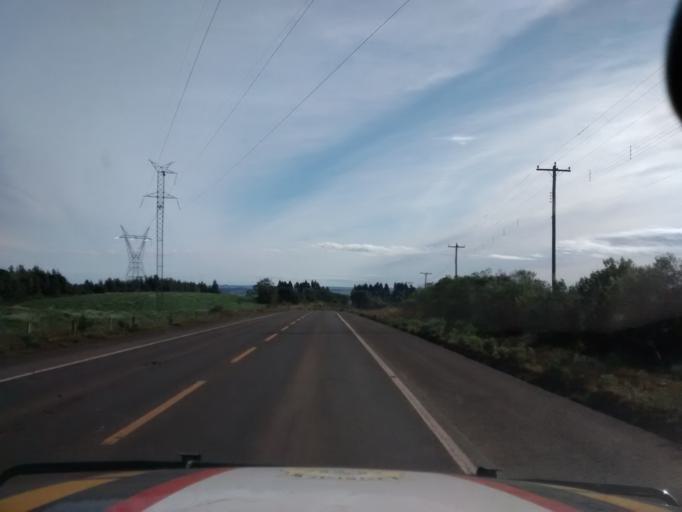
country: BR
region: Rio Grande do Sul
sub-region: Lagoa Vermelha
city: Lagoa Vermelha
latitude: -28.1818
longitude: -51.5239
